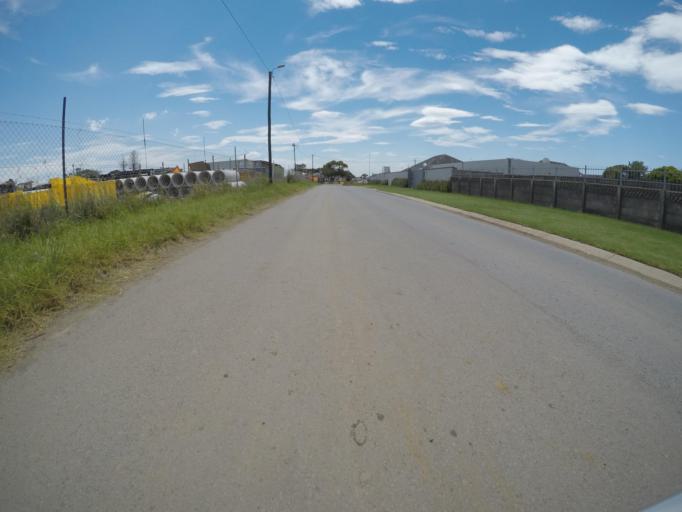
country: ZA
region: Eastern Cape
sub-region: Buffalo City Metropolitan Municipality
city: East London
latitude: -33.0368
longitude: 27.8509
